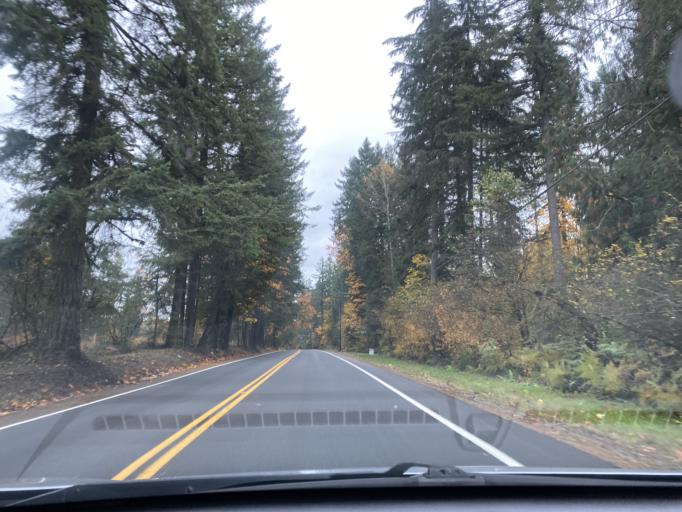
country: US
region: Washington
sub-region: King County
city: Lake Morton-Berrydale
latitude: 47.3000
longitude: -122.0953
